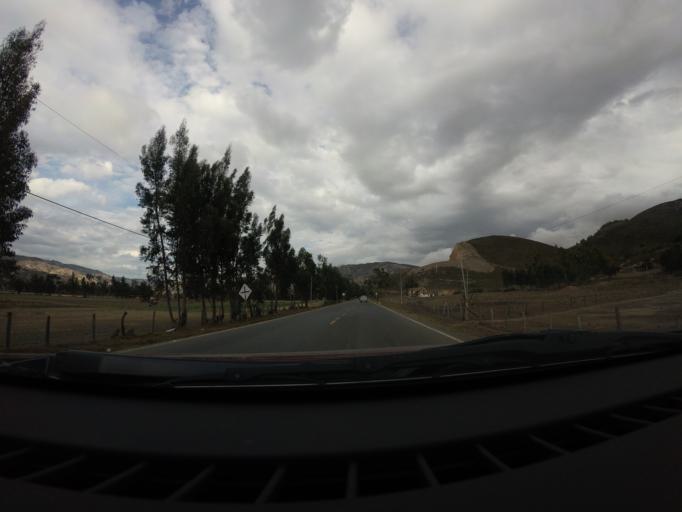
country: CO
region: Boyaca
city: Cucaita
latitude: 5.5422
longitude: -73.4675
